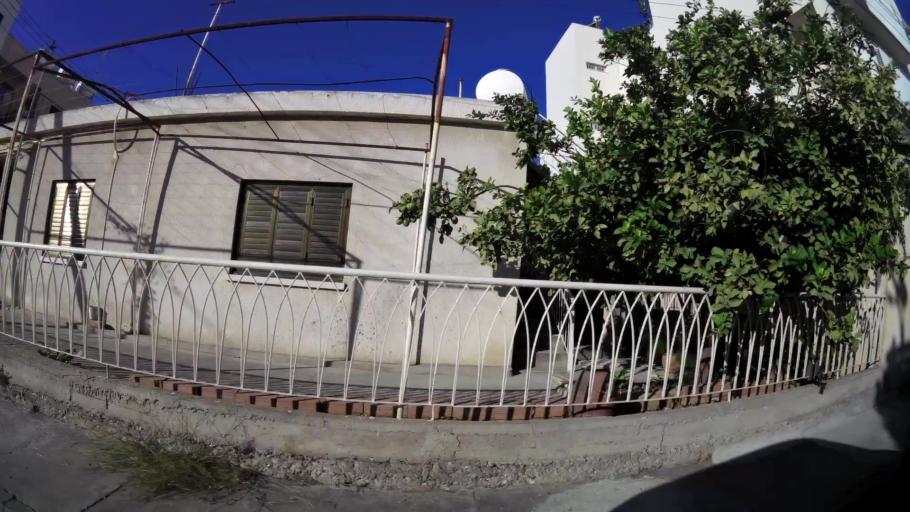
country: CY
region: Larnaka
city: Larnaca
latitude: 34.9199
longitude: 33.6211
